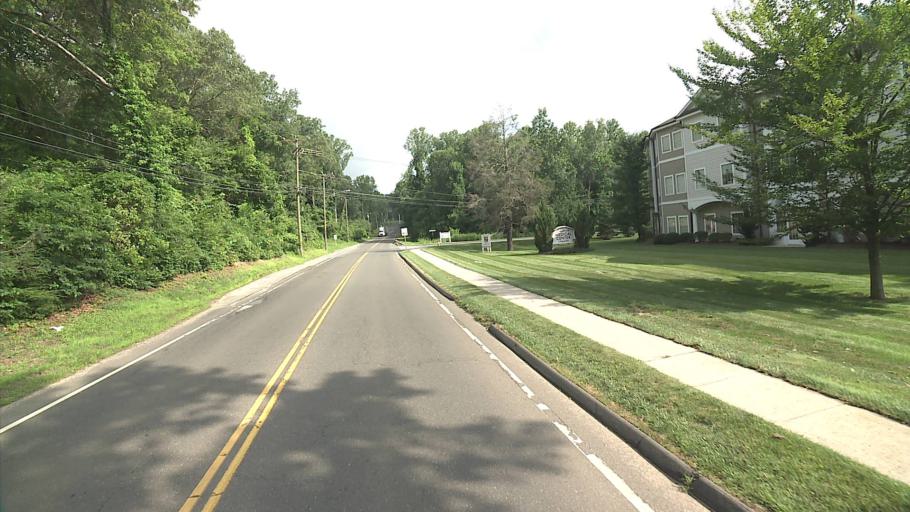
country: US
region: Connecticut
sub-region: Middlesex County
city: Clinton
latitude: 41.2951
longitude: -72.4893
